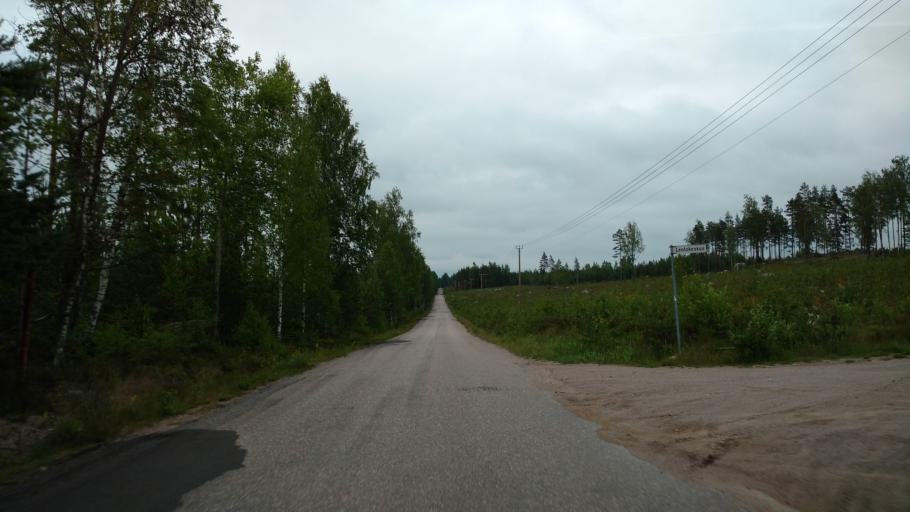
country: FI
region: Varsinais-Suomi
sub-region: Salo
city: Kiikala
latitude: 60.4655
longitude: 23.6443
